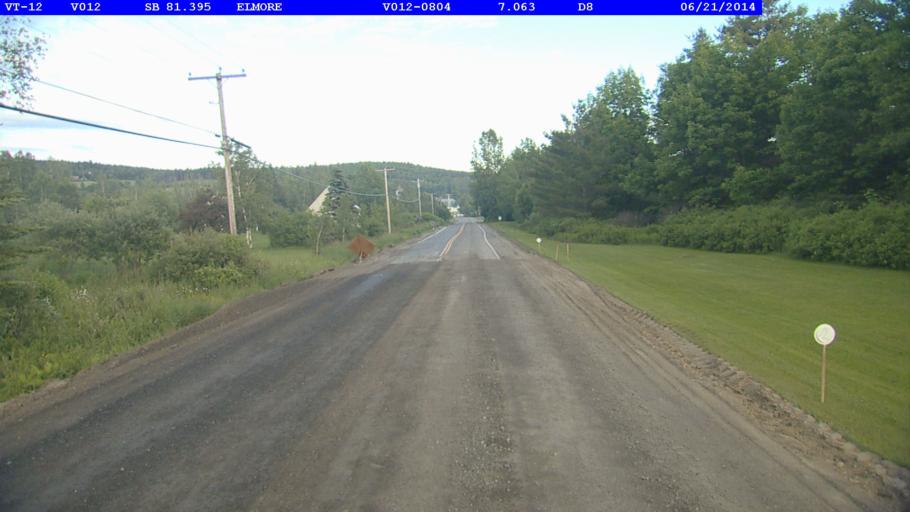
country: US
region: Vermont
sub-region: Lamoille County
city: Morrisville
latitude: 44.5443
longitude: -72.5273
